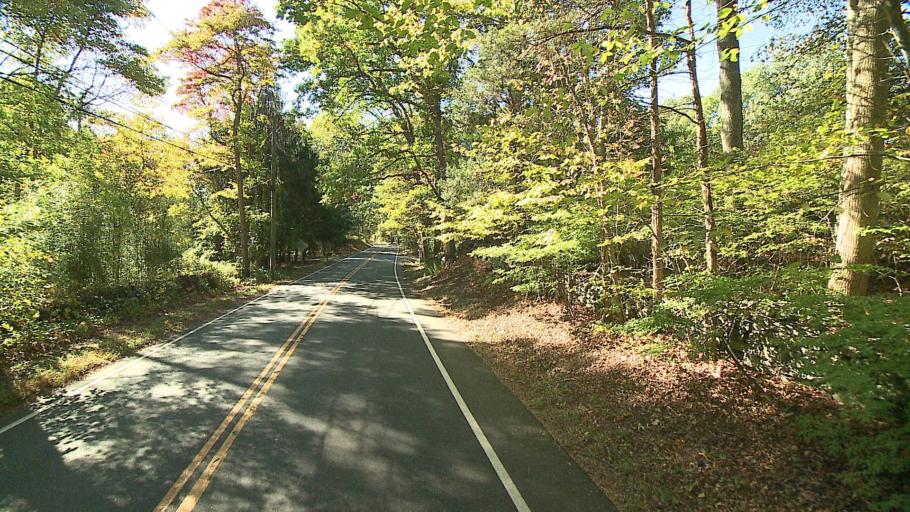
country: US
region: Connecticut
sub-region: Fairfield County
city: Trumbull
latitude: 41.2568
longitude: -73.3017
